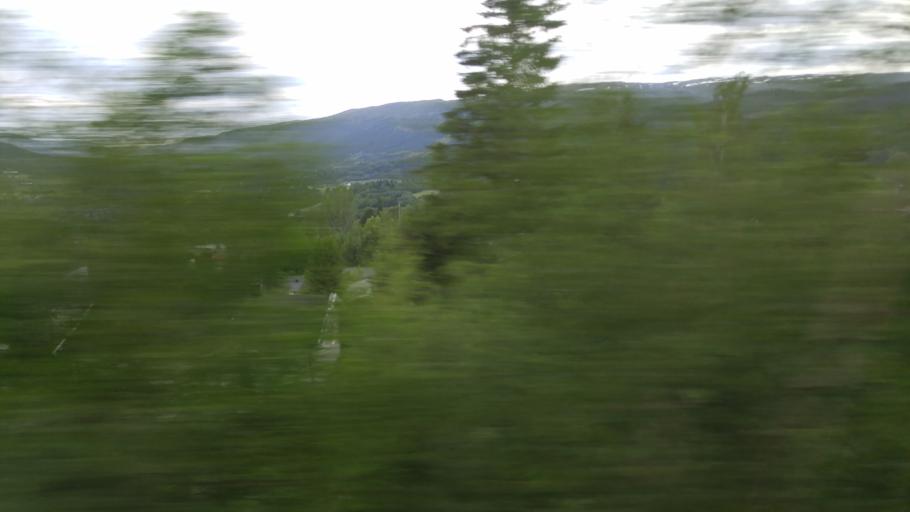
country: NO
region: Nord-Trondelag
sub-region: Meraker
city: Meraker
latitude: 63.4194
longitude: 11.7564
